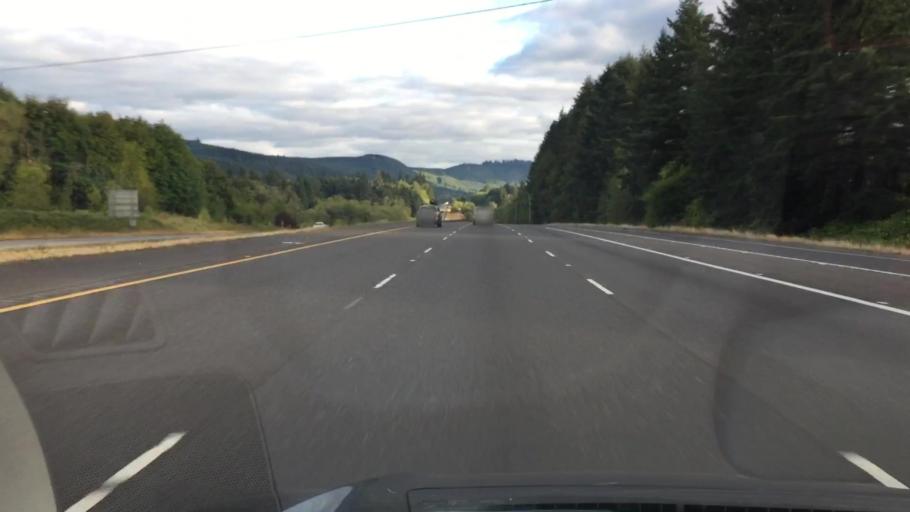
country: US
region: Washington
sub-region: Cowlitz County
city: Castle Rock
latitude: 46.2813
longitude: -122.9011
